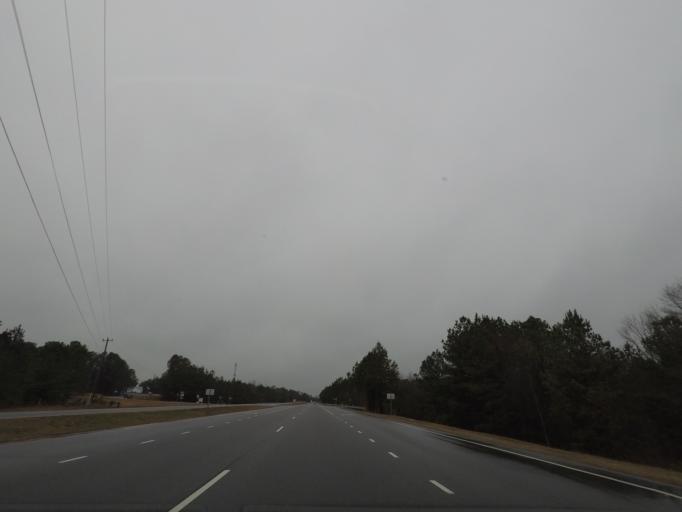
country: US
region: North Carolina
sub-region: Lee County
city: Broadway
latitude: 35.3379
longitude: -79.0979
